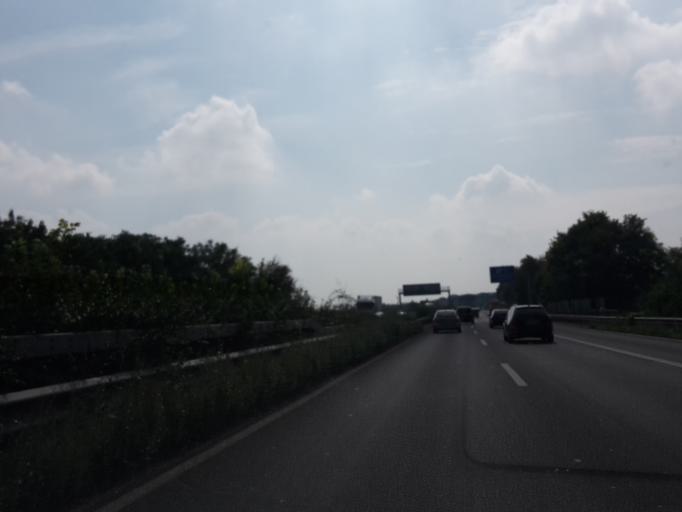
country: DE
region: Rheinland-Pfalz
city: Klein-Winternheim
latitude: 49.9558
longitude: 8.2292
